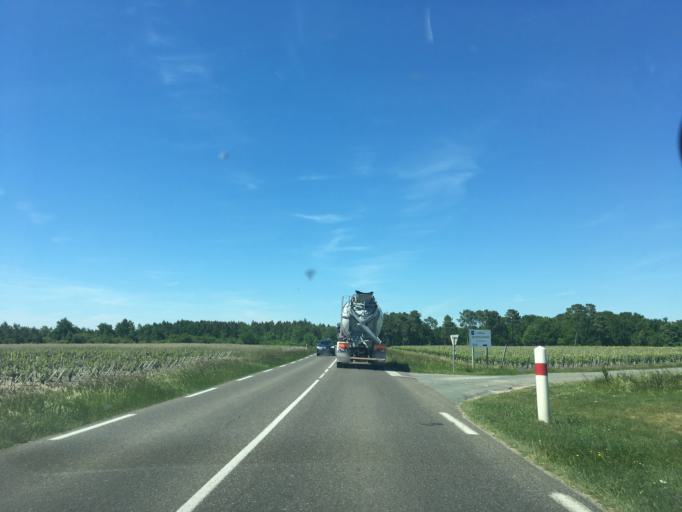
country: FR
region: Aquitaine
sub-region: Departement de la Gironde
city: Listrac-Medoc
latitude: 45.0895
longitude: -0.7975
